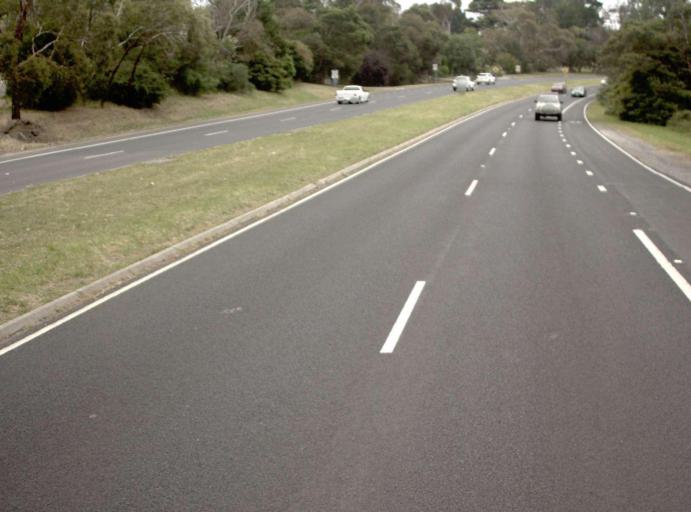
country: AU
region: Victoria
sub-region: Mornington Peninsula
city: Mount Eliza
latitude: -38.1816
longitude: 145.0961
